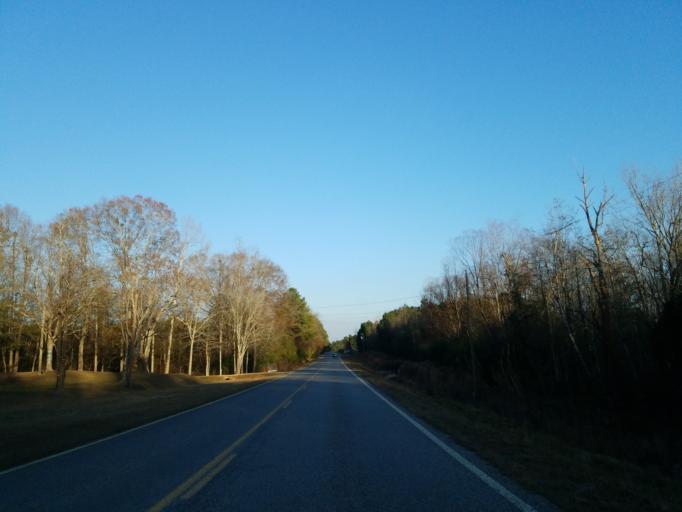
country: US
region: Mississippi
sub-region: Clarke County
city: Stonewall
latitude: 32.1667
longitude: -88.8556
